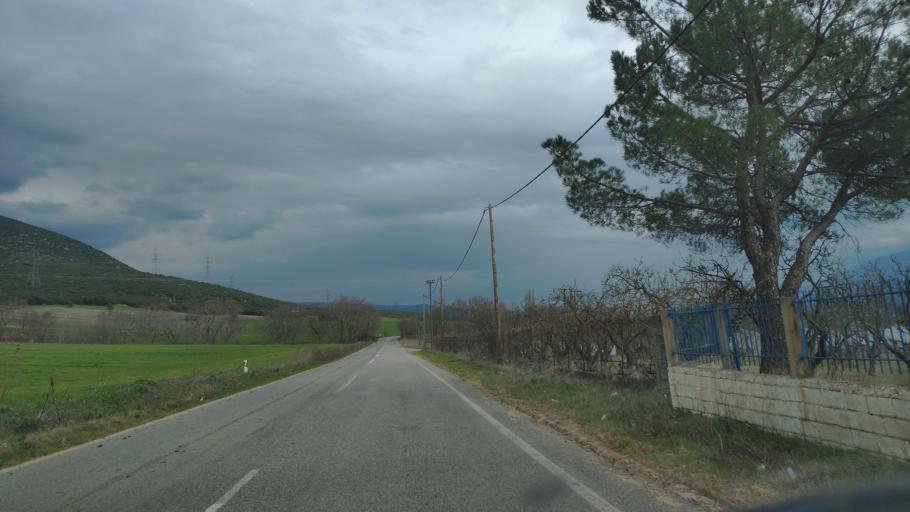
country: GR
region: Central Greece
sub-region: Nomos Fthiotidos
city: Amfikleia
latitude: 38.7069
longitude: 22.4983
